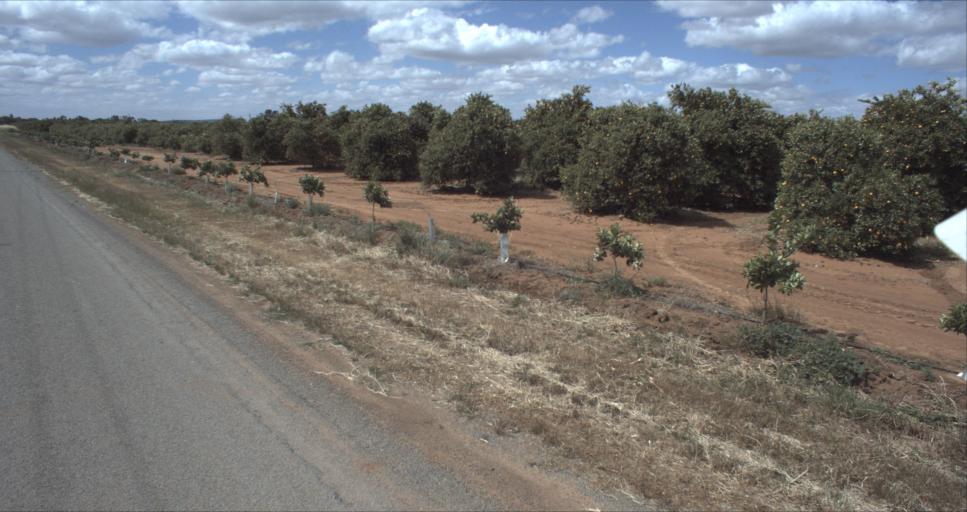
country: AU
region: New South Wales
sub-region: Leeton
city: Leeton
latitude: -34.5840
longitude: 146.3917
